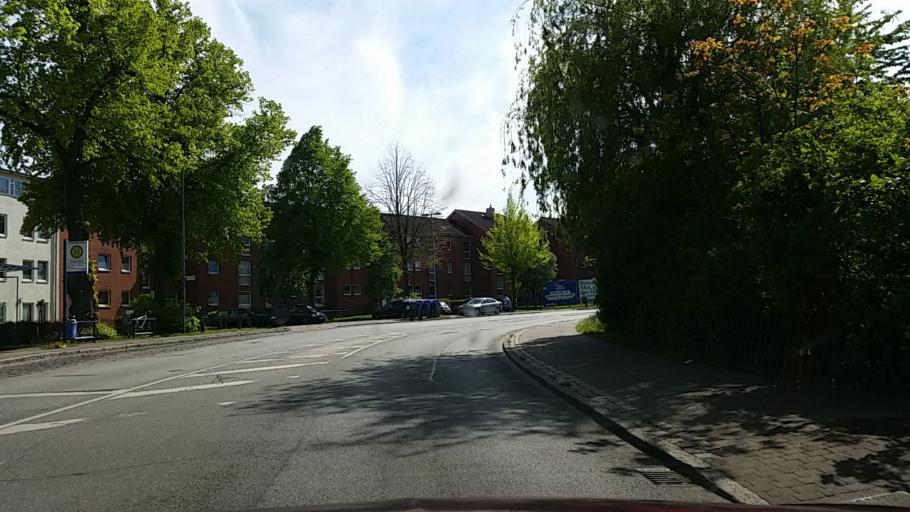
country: DE
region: Schleswig-Holstein
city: Luebeck
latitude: 53.8509
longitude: 10.6589
